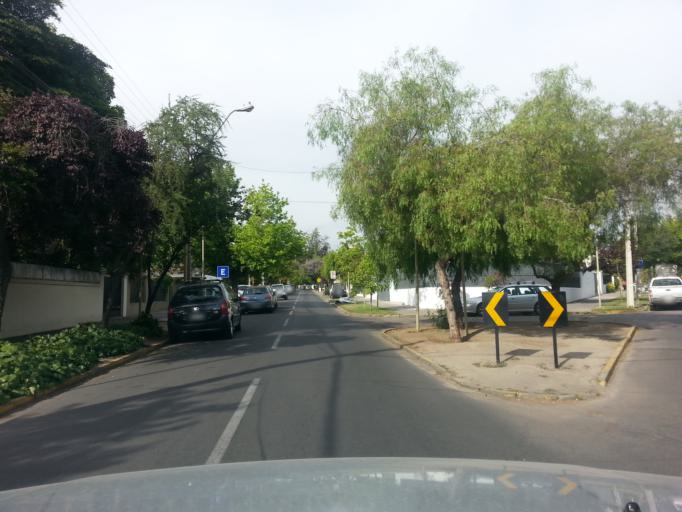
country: CL
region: Santiago Metropolitan
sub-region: Provincia de Santiago
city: Villa Presidente Frei, Nunoa, Santiago, Chile
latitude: -33.4231
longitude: -70.5914
